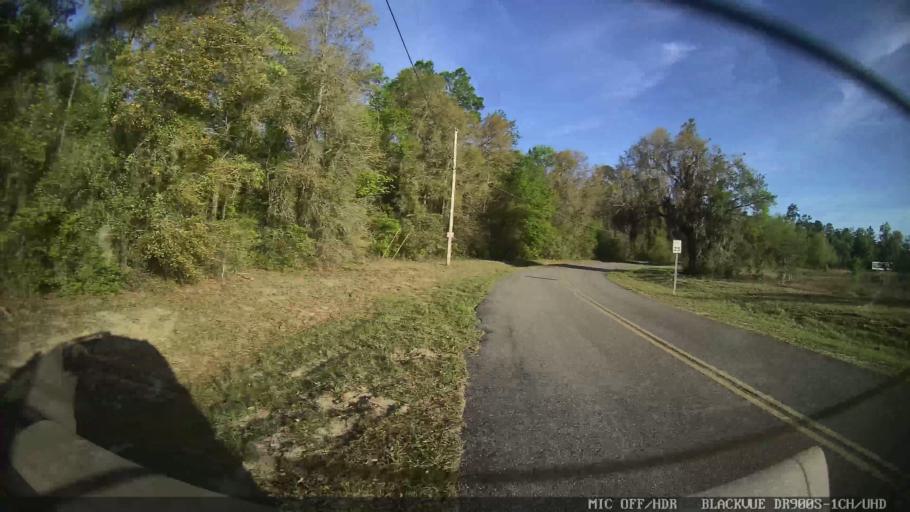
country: US
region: Georgia
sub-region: Echols County
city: Statenville
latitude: 30.6454
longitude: -83.1806
